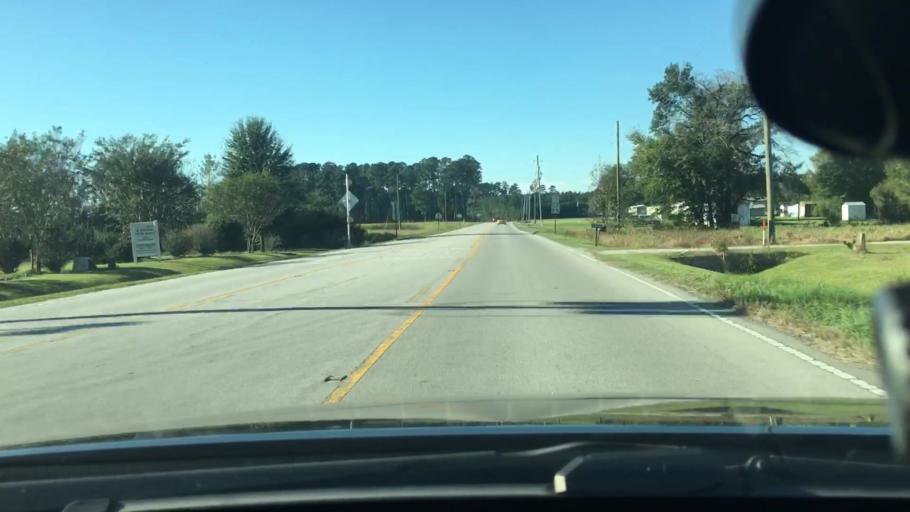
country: US
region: North Carolina
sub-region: Pitt County
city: Windsor
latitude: 35.4649
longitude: -77.2755
